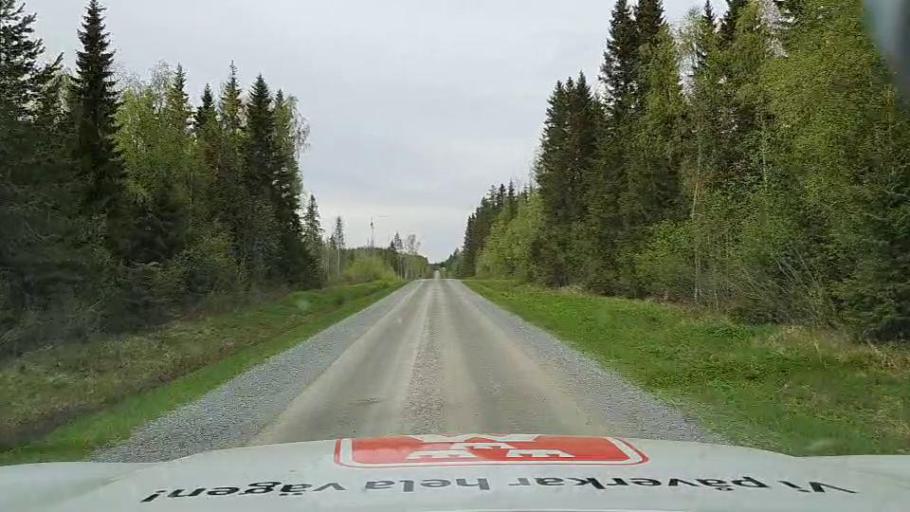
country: SE
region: Jaemtland
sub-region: OEstersunds Kommun
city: Brunflo
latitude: 62.6230
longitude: 14.9438
